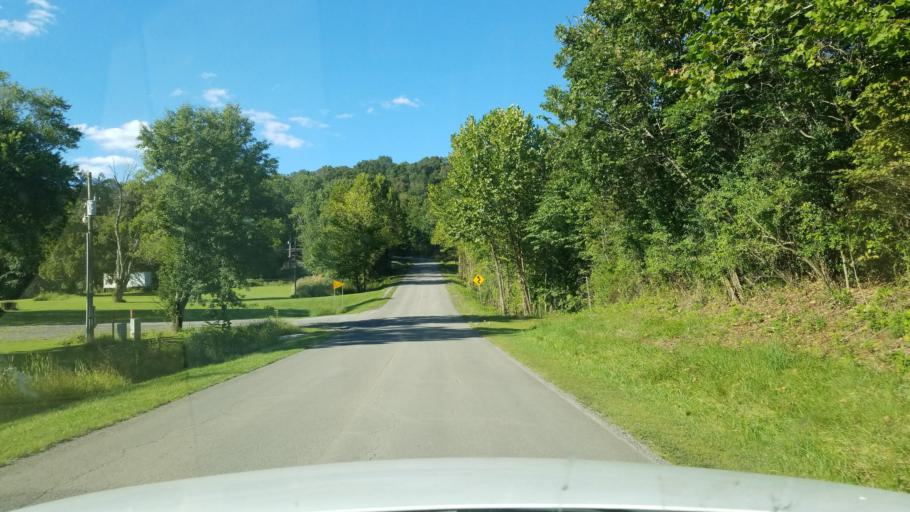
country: US
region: Illinois
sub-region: Hardin County
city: Elizabethtown
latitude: 37.5953
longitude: -88.3646
